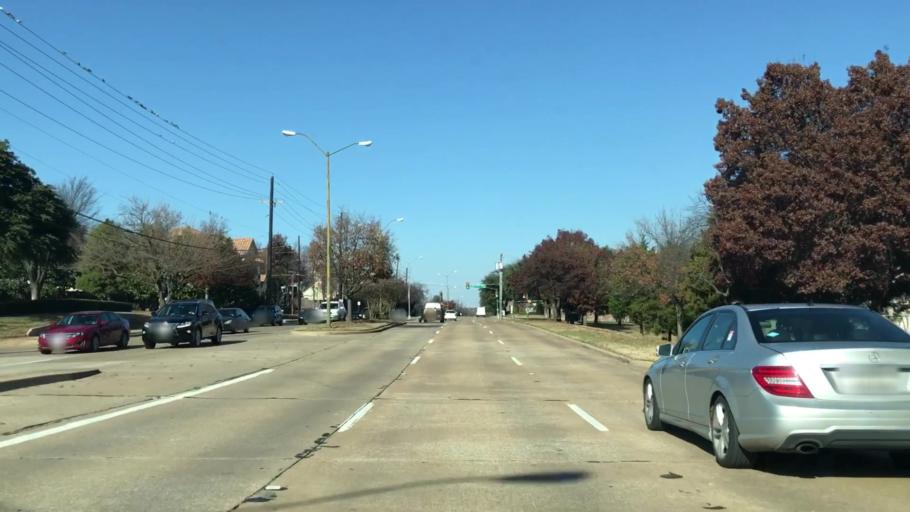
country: US
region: Texas
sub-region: Dallas County
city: Addison
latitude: 32.9158
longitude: -96.7863
